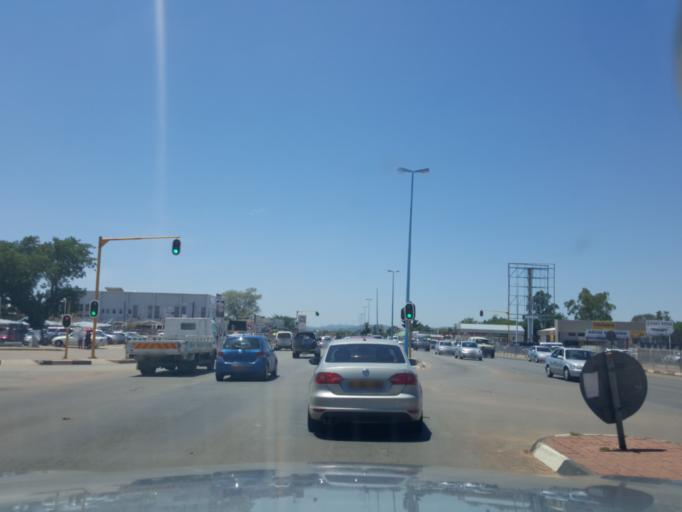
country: BW
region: Kweneng
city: Mogoditshane
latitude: -24.6285
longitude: 25.8716
